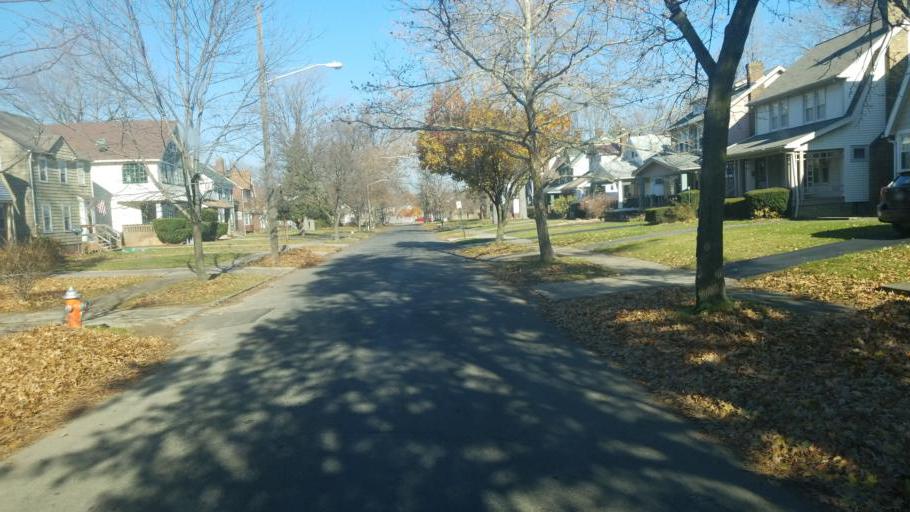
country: US
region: Ohio
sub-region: Cuyahoga County
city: Cleveland Heights
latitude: 41.5328
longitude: -81.5510
